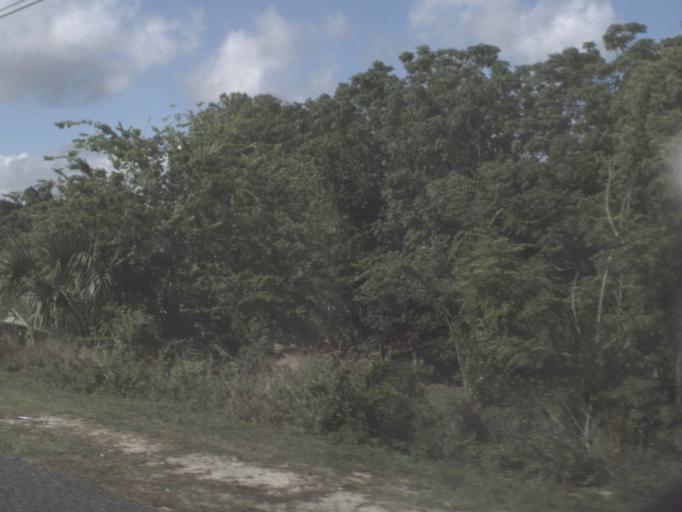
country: US
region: Florida
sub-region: Lake County
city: Fruitland Park
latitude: 28.8914
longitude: -81.9073
